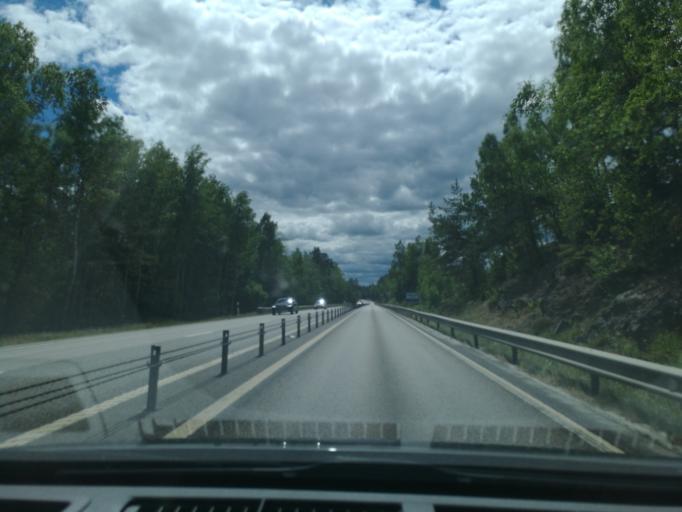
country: SE
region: OEstergoetland
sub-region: Norrkopings Kommun
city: Jursla
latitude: 58.7484
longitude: 16.1756
